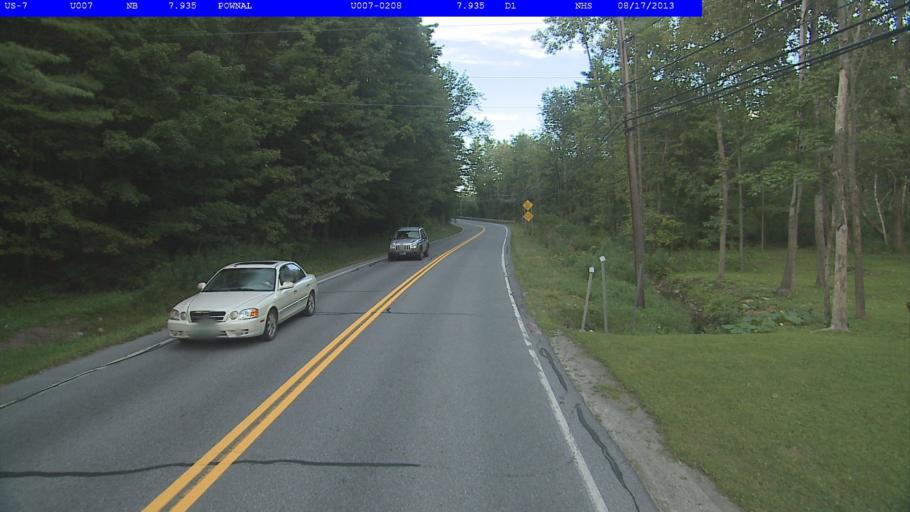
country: US
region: Vermont
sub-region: Bennington County
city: Bennington
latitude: 42.8369
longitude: -73.1990
